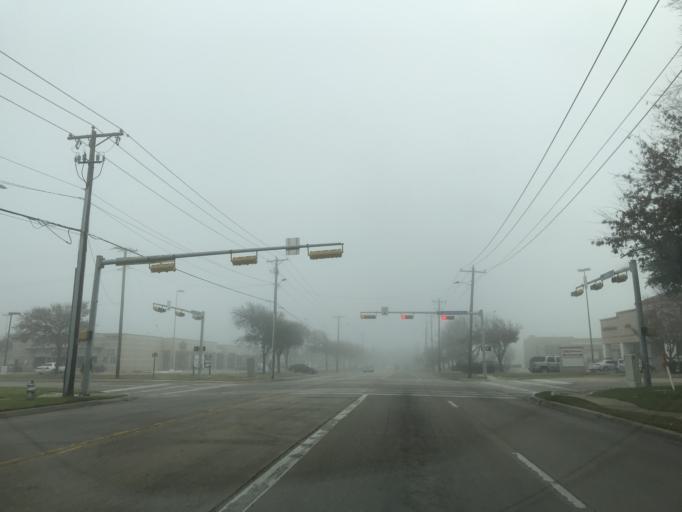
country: US
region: Texas
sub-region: Tarrant County
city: Arlington
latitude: 32.7730
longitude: -97.0834
